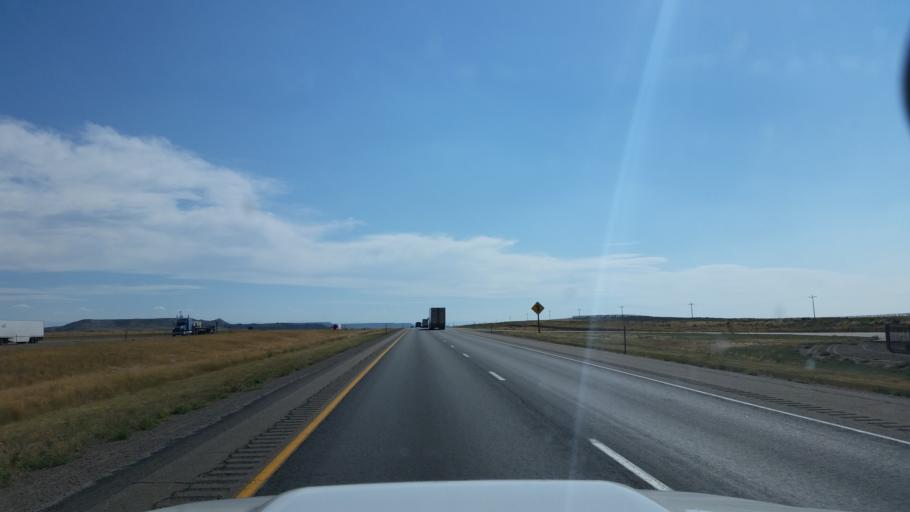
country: US
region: Wyoming
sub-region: Uinta County
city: Lyman
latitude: 41.4930
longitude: -110.0146
